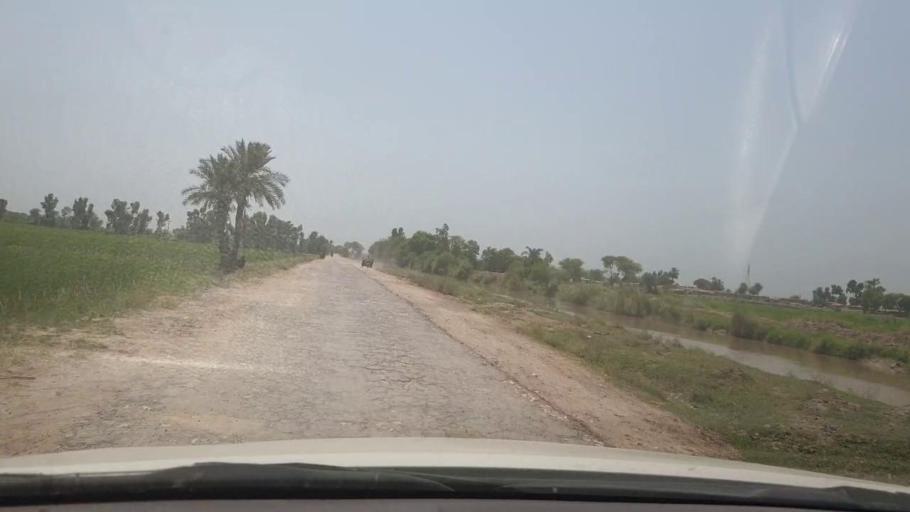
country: PK
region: Sindh
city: Shikarpur
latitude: 28.0990
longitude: 68.5805
